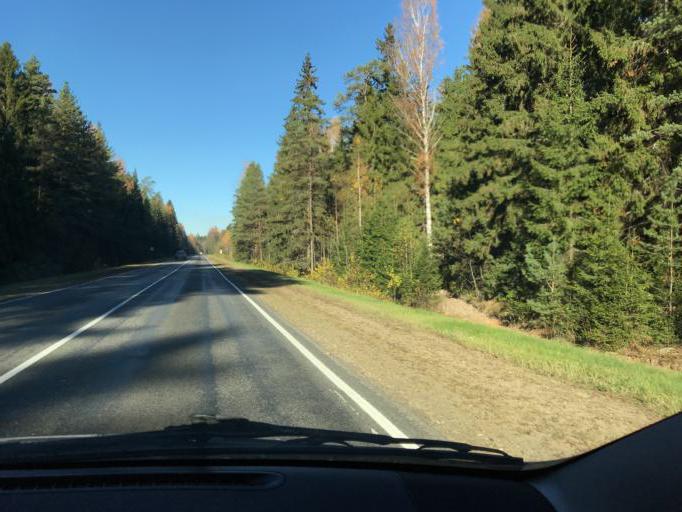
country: BY
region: Vitebsk
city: Polatsk
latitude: 55.4132
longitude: 28.7976
